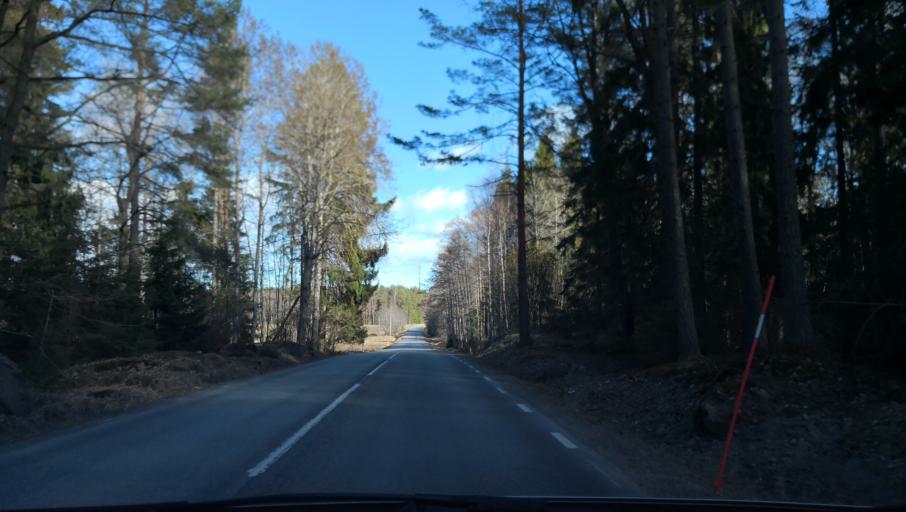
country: SE
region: Stockholm
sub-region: Varmdo Kommun
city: Hemmesta
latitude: 59.3569
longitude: 18.5723
